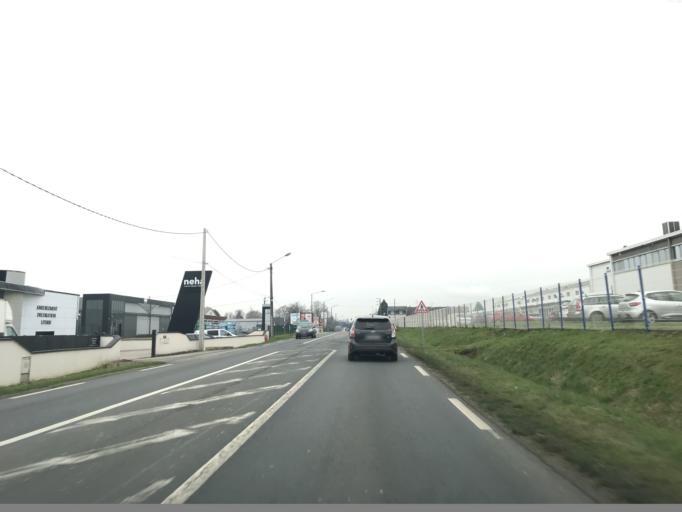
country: FR
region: Haute-Normandie
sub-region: Departement de la Seine-Maritime
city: Boos
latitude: 49.3967
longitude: 1.1808
